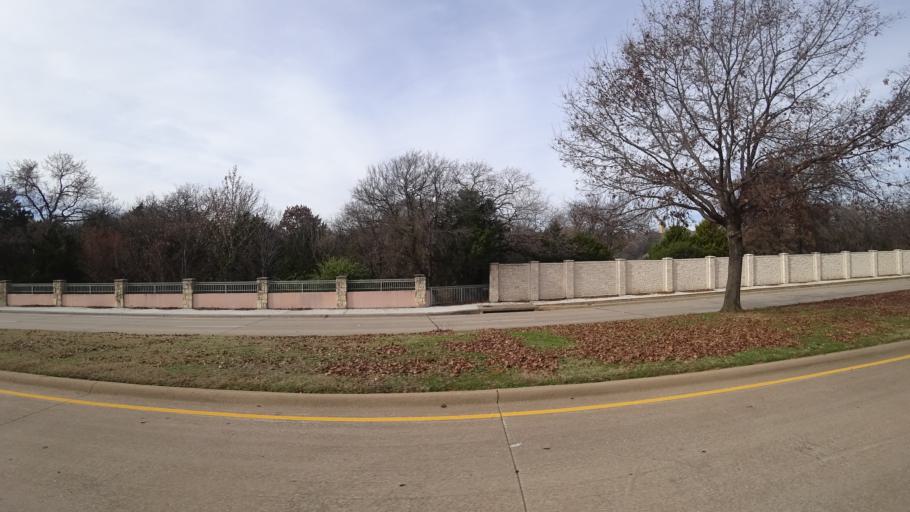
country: US
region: Texas
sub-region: Denton County
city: Highland Village
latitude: 33.0799
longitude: -97.0359
